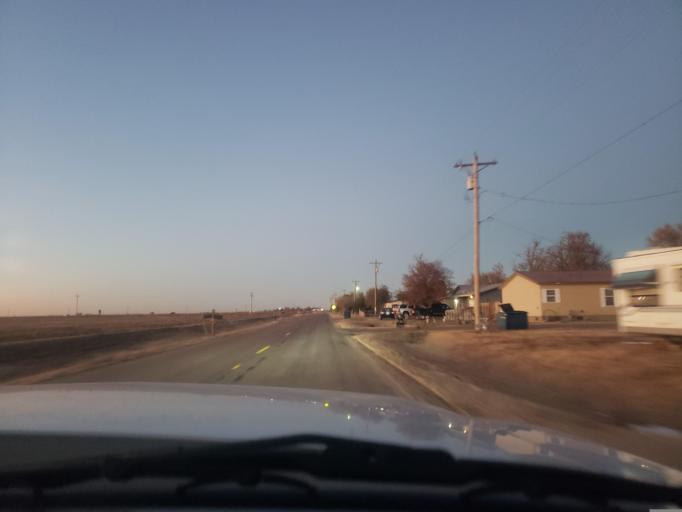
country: US
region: Kansas
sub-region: Finney County
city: Garden City
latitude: 37.9985
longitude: -100.8749
